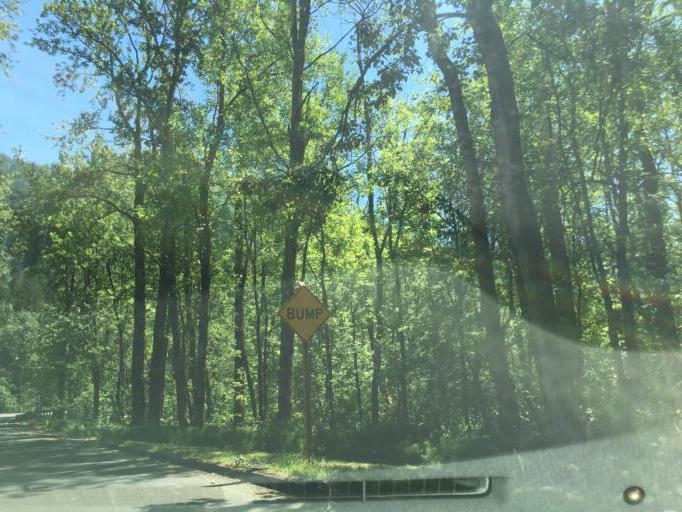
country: US
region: Washington
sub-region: Clark County
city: Washougal
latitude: 45.5725
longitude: -122.1589
